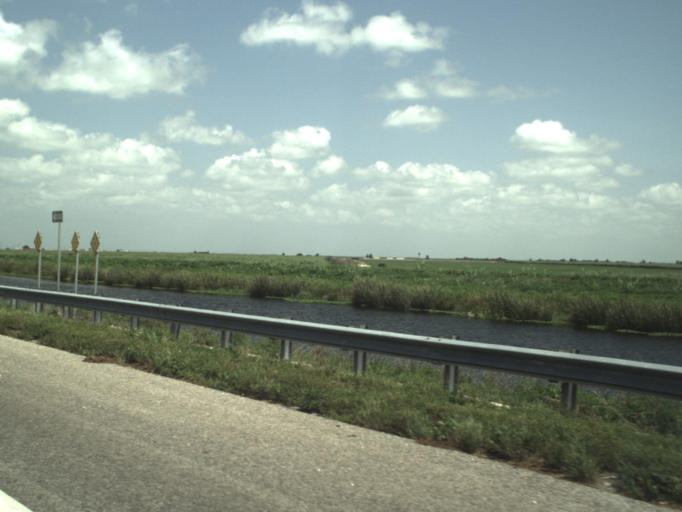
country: US
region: Florida
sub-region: Palm Beach County
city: Belle Glade Camp
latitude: 26.5484
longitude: -80.7032
